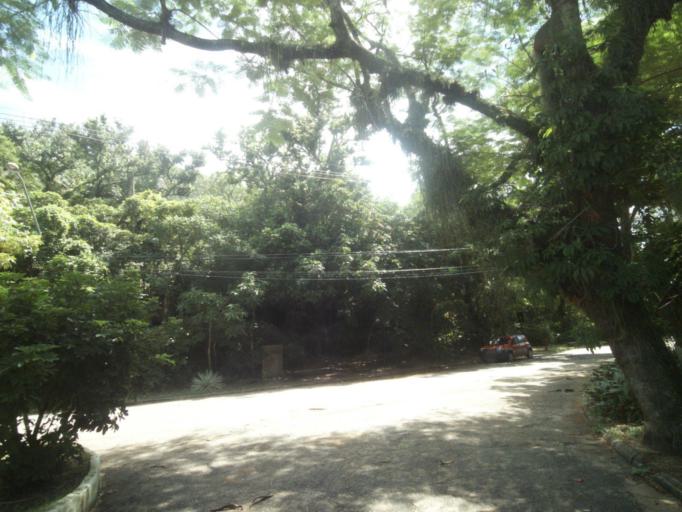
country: BR
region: Rio de Janeiro
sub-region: Niteroi
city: Niteroi
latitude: -22.9716
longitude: -43.0349
